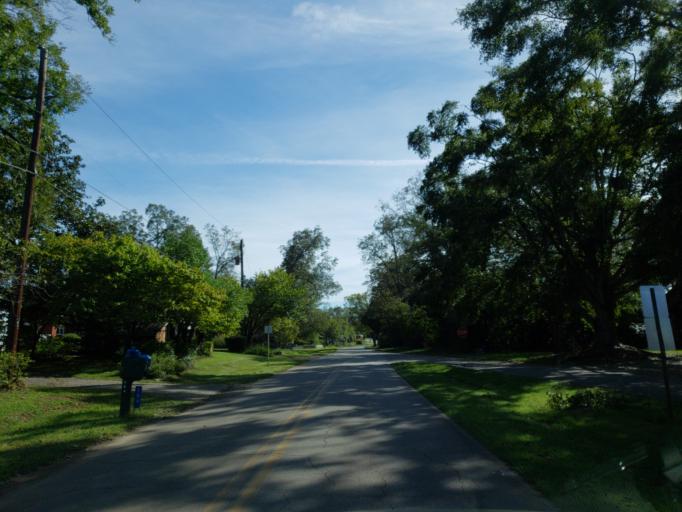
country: US
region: Georgia
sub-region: Crawford County
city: Roberta
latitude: 32.8675
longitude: -84.0927
